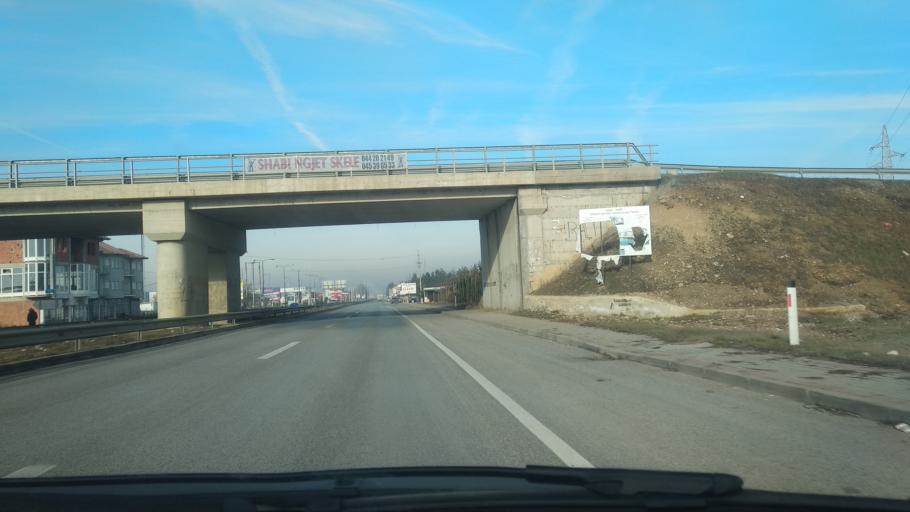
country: XK
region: Pristina
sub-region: Komuna e Obiliqit
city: Obiliq
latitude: 42.7174
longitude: 21.0935
